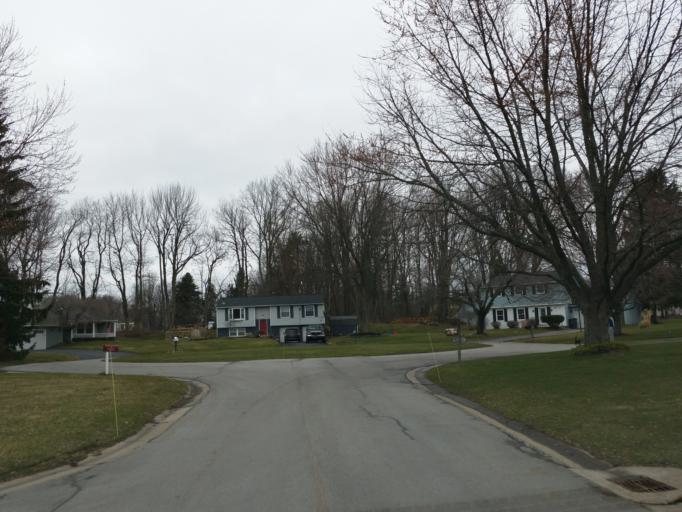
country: US
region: New York
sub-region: Monroe County
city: Scottsville
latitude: 43.1106
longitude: -77.7590
